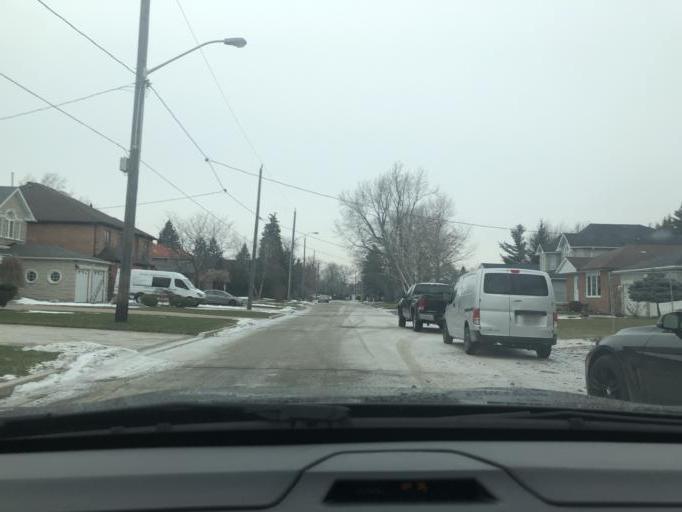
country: CA
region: Ontario
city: Scarborough
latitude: 43.7834
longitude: -79.2710
